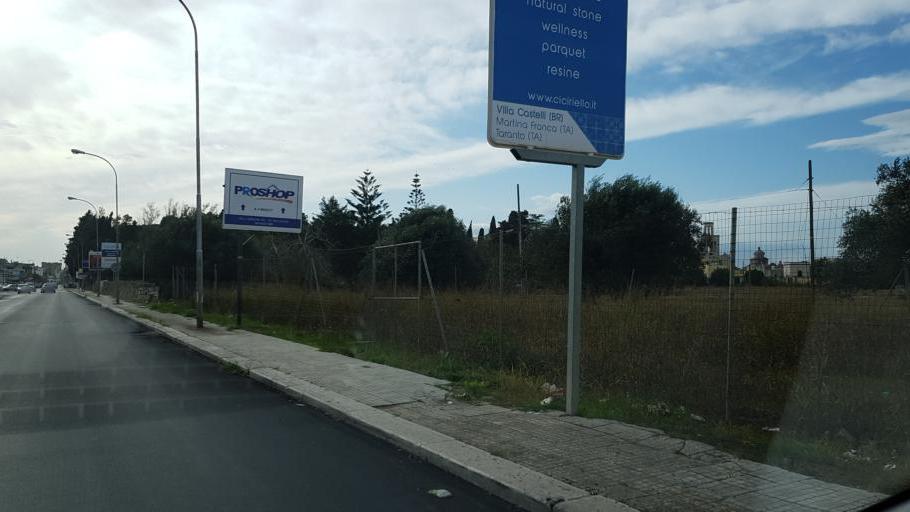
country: IT
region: Apulia
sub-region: Provincia di Brindisi
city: Mesagne
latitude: 40.5655
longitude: 17.8160
